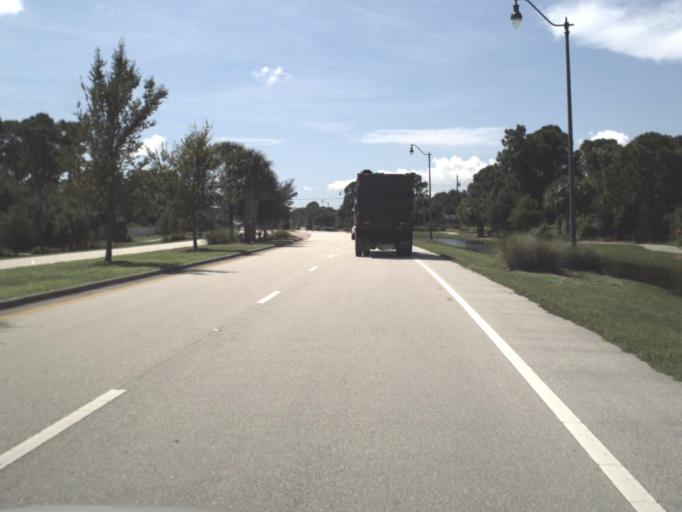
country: US
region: Florida
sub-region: Sarasota County
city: North Port
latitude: 27.0378
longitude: -82.1635
